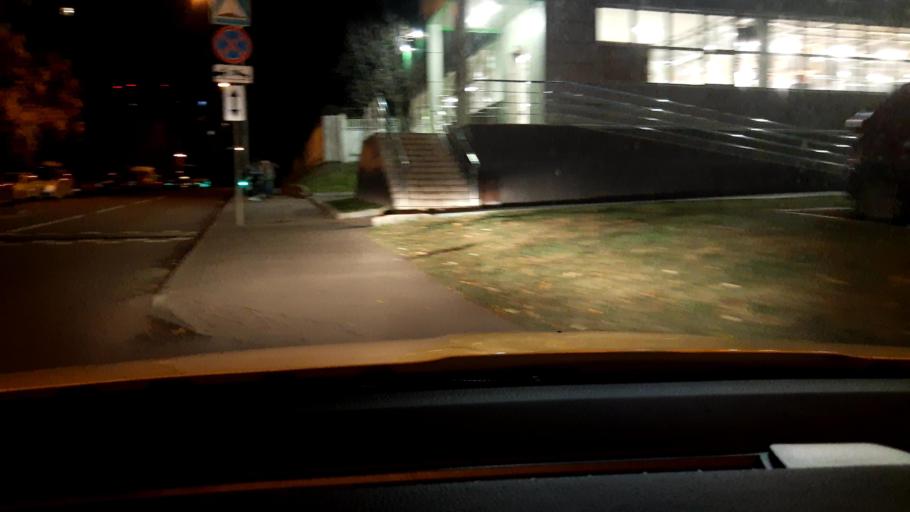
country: RU
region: Moscow
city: Strogino
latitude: 55.8569
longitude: 37.4074
